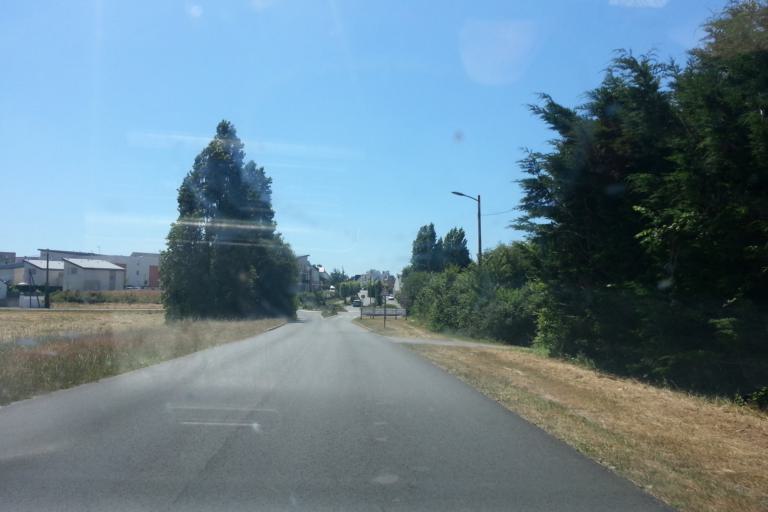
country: FR
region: Brittany
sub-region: Departement du Morbihan
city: Locmiquelic
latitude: 47.7206
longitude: -3.3342
